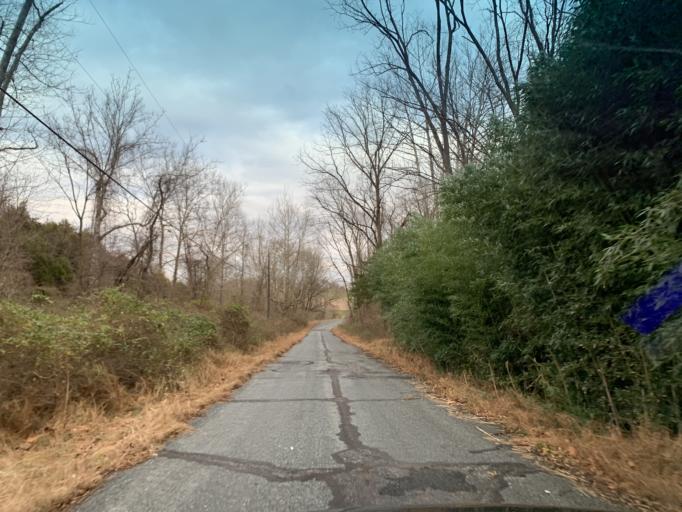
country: US
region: Maryland
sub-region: Harford County
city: Jarrettsville
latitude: 39.6612
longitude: -76.4514
